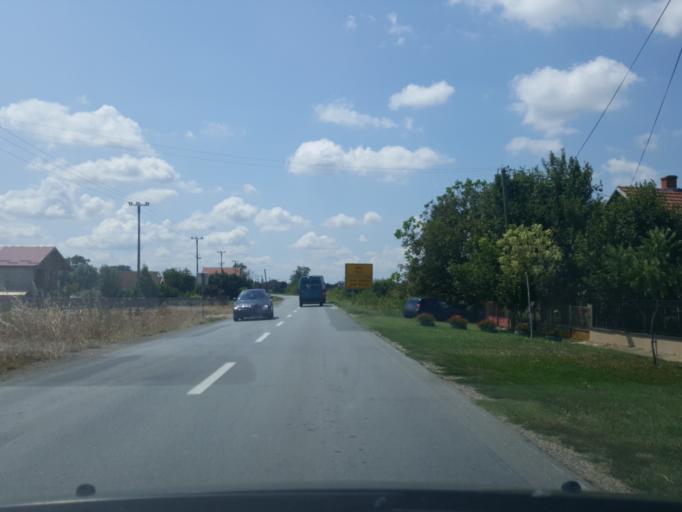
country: RS
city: Salas Nocajski
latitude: 44.9421
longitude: 19.5772
